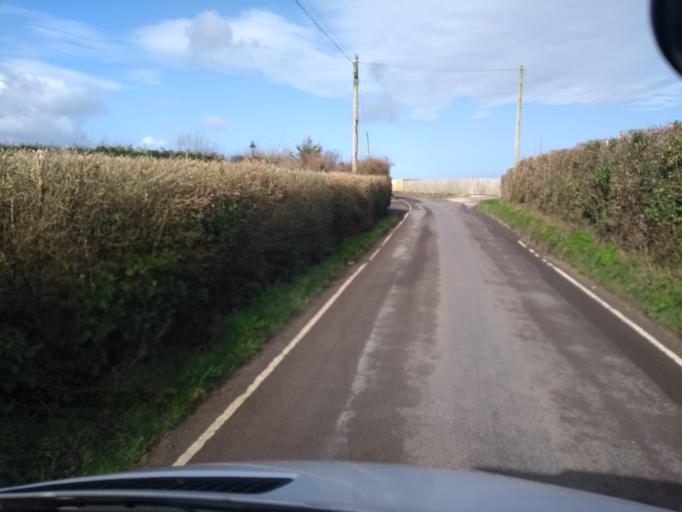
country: GB
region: England
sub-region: Somerset
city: Woolavington
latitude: 51.1610
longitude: -2.9273
